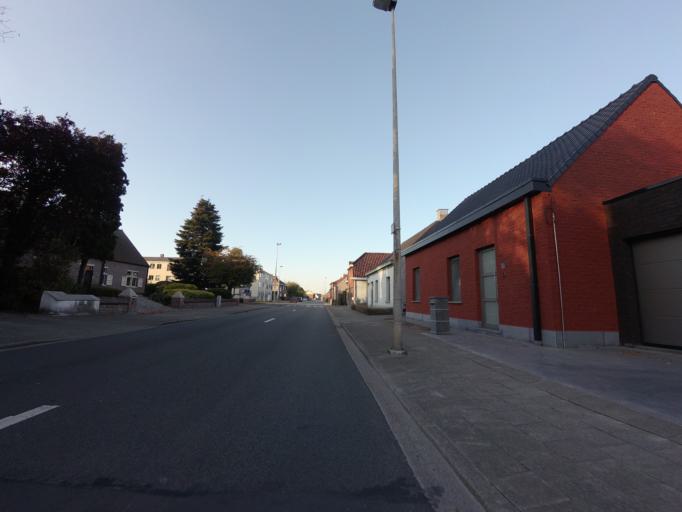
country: BE
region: Flanders
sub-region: Provincie Antwerpen
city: Stabroek
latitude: 51.3453
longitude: 4.3136
